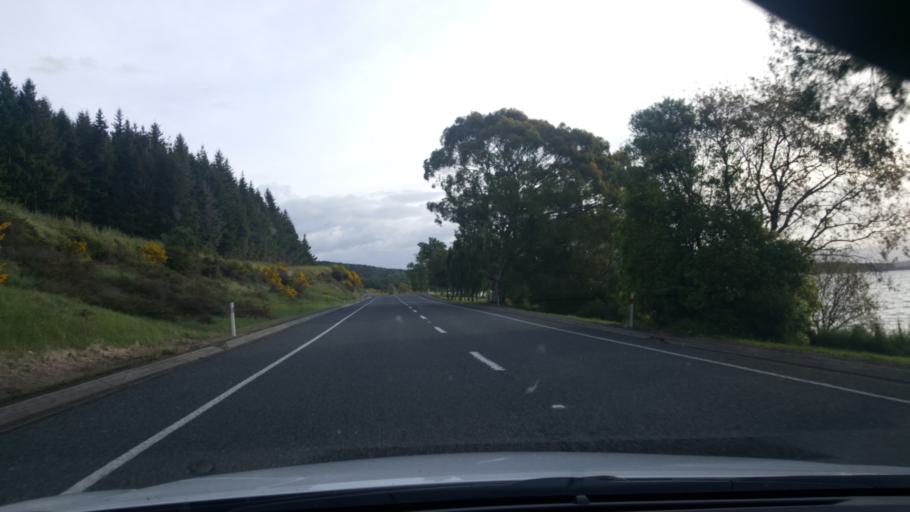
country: NZ
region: Waikato
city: Turangi
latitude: -38.8962
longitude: 175.9469
